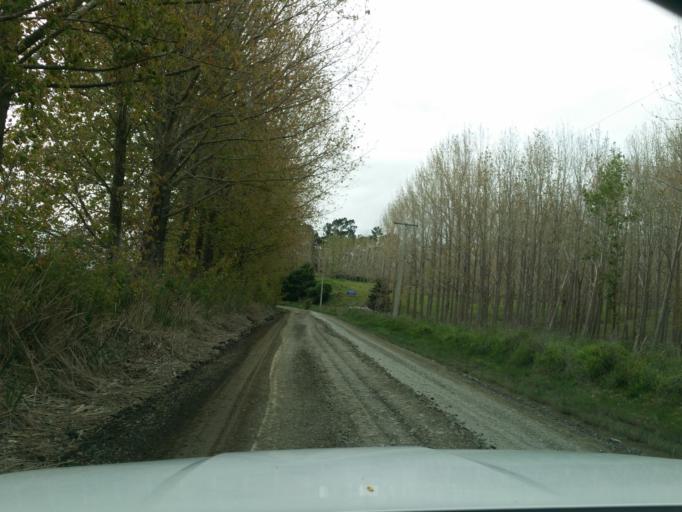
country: NZ
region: Northland
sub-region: Kaipara District
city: Dargaville
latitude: -35.9198
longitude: 173.9218
